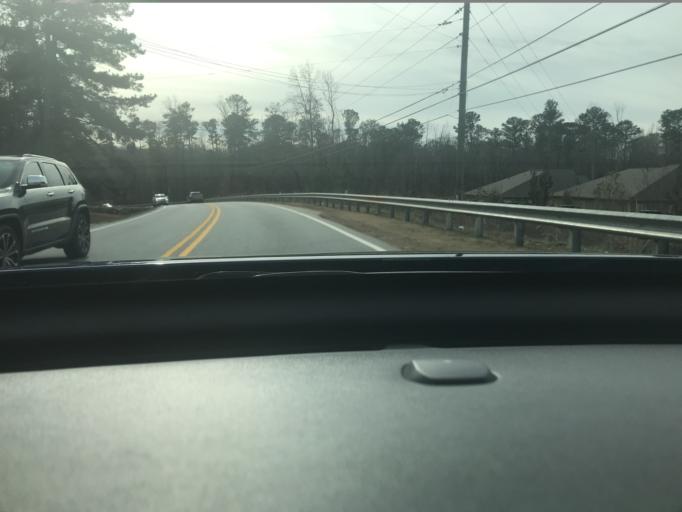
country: US
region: Georgia
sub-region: Gwinnett County
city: Mountain Park
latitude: 33.8647
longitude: -84.0974
